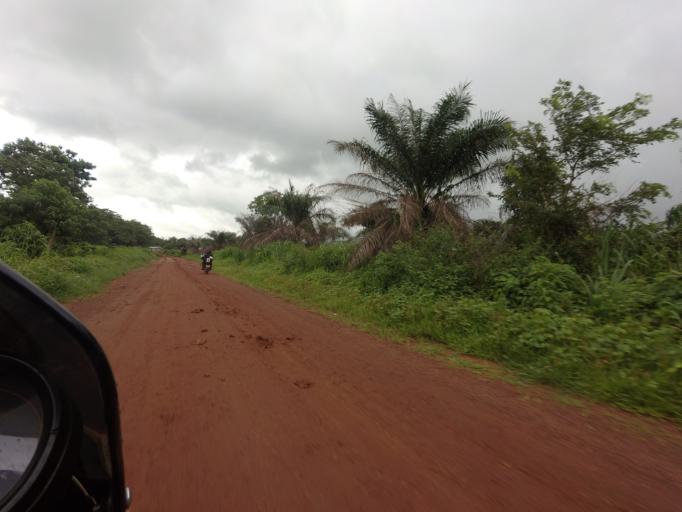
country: SL
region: Northern Province
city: Kukuna
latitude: 9.2710
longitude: -12.7128
